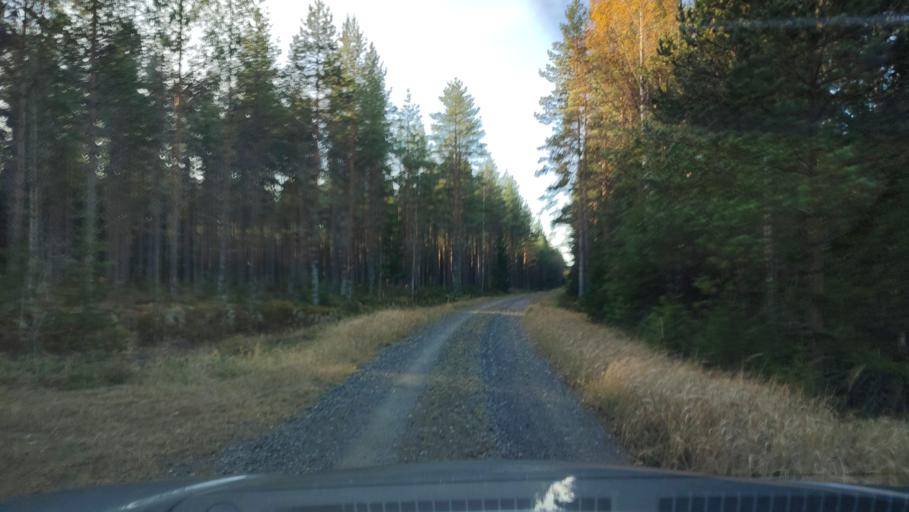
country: FI
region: Southern Ostrobothnia
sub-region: Suupohja
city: Karijoki
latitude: 62.1985
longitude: 21.6127
